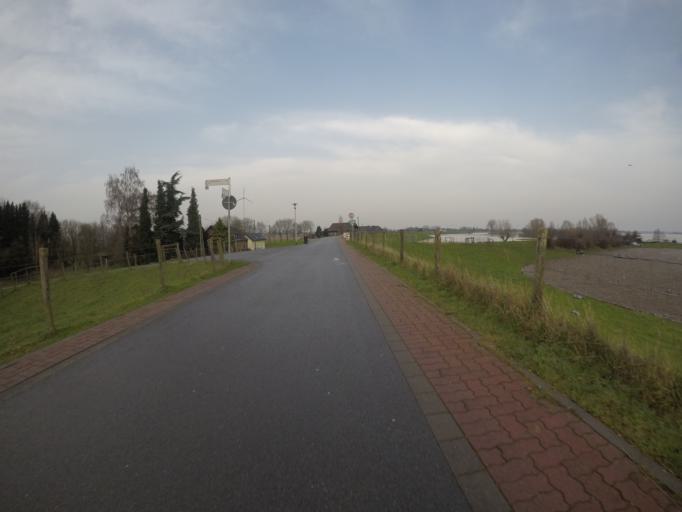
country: DE
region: North Rhine-Westphalia
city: Rees
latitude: 51.7181
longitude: 6.4030
